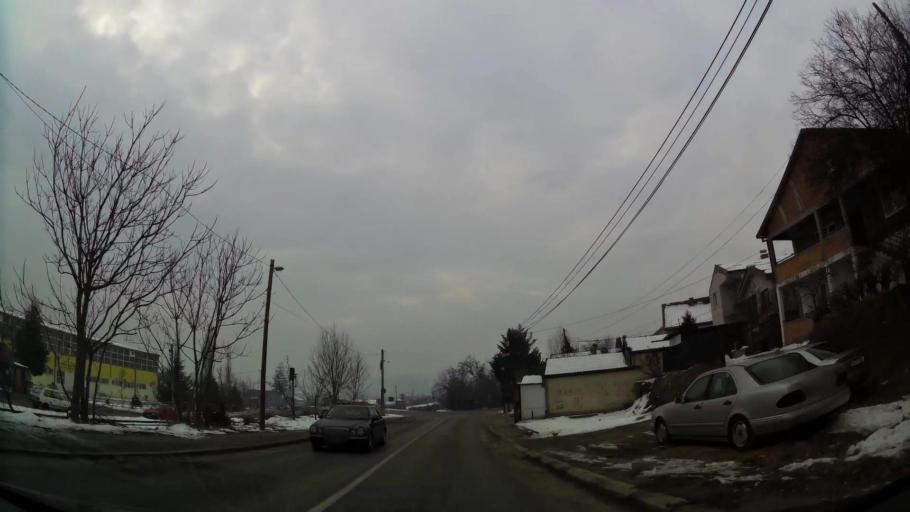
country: MK
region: Saraj
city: Saraj
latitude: 42.0319
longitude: 21.3485
